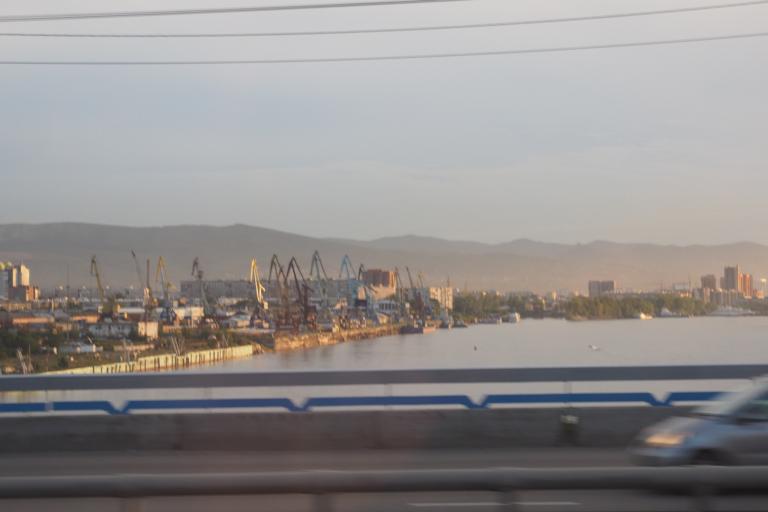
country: RU
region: Krasnoyarskiy
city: Krasnoyarsk
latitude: 56.0191
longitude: 92.9513
